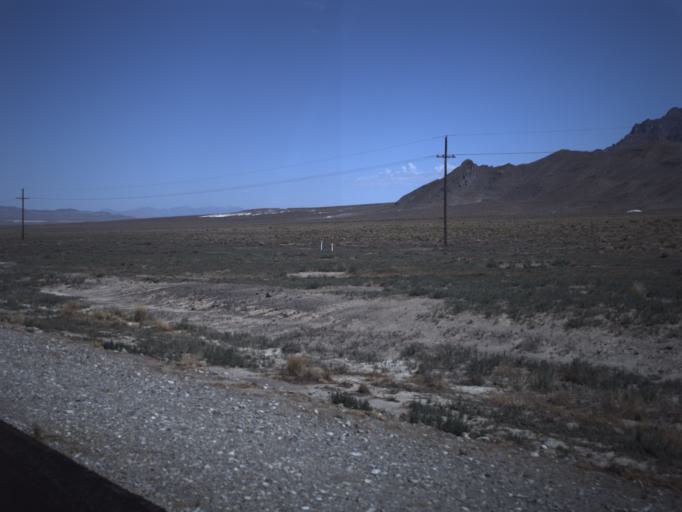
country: US
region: Utah
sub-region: Beaver County
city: Milford
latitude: 39.0521
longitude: -113.4223
